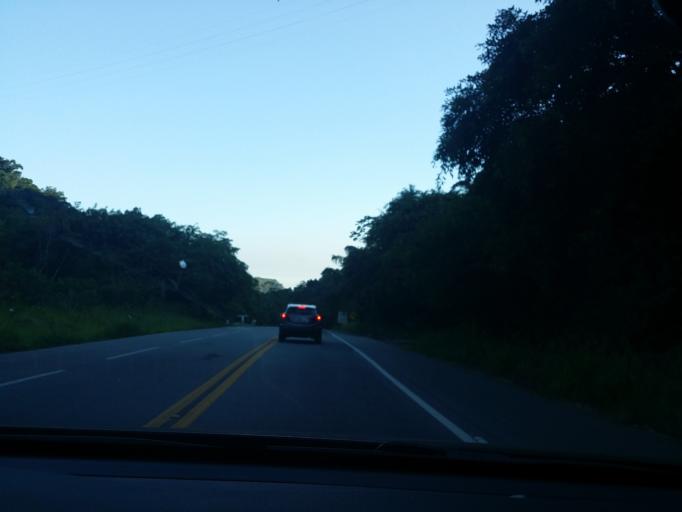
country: BR
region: Sao Paulo
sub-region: Sao Sebastiao
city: Sao Sebastiao
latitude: -23.7450
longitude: -45.7292
